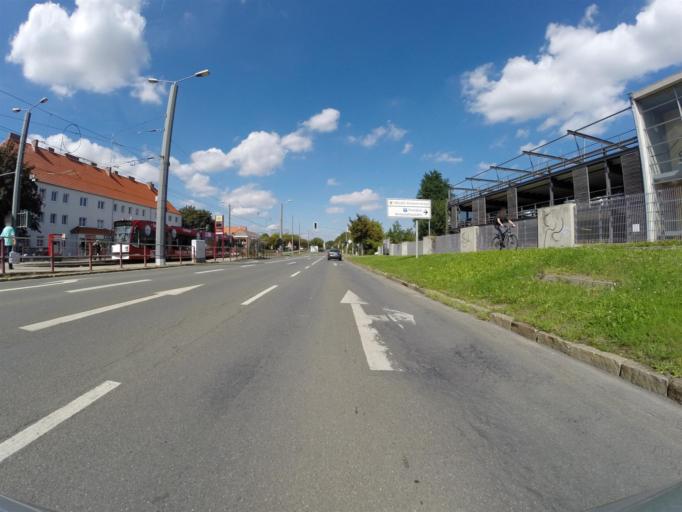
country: DE
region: Thuringia
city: Erfurt
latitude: 50.9948
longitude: 11.0094
